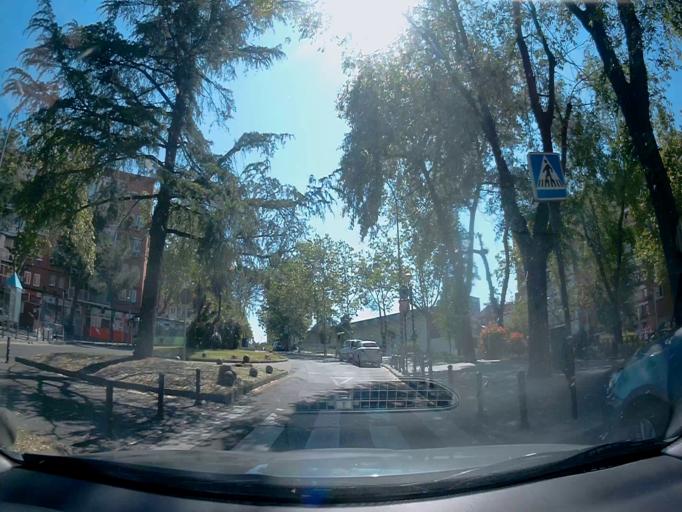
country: ES
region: Madrid
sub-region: Provincia de Madrid
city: Alcorcon
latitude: 40.3429
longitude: -3.8297
